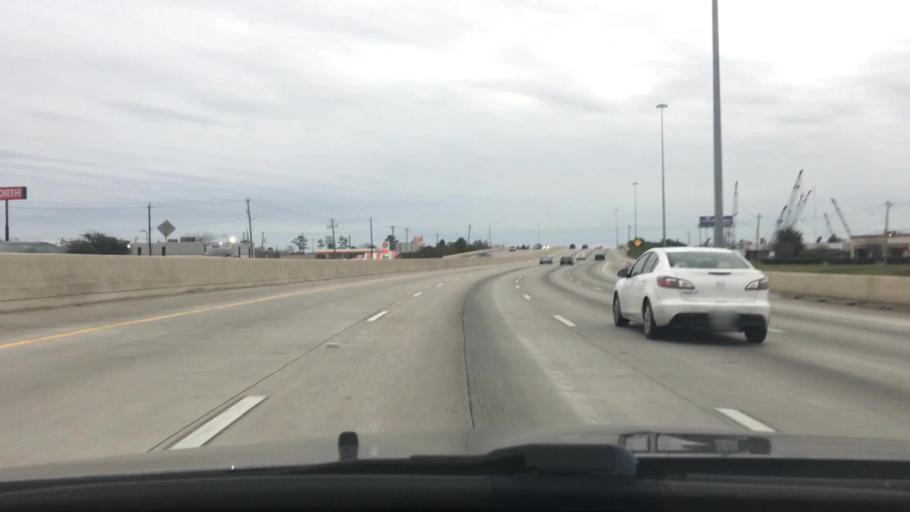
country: US
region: Texas
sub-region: Harris County
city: Houston
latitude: 29.8089
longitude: -95.3052
